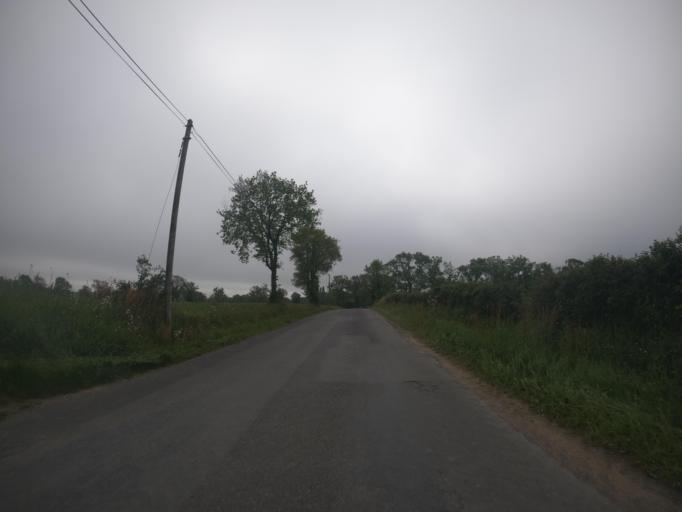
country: FR
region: Poitou-Charentes
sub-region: Departement des Deux-Sevres
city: Chiche
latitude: 46.8845
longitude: -0.3306
